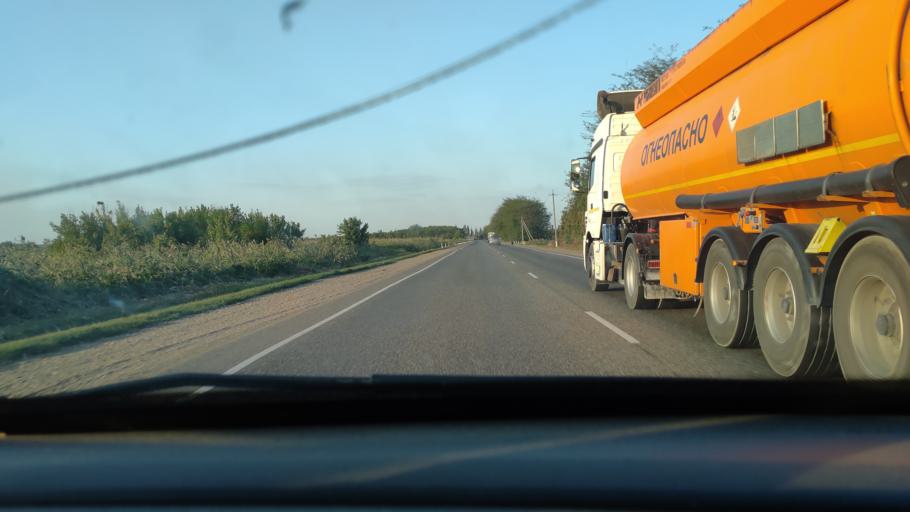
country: RU
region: Krasnodarskiy
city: Kanevskaya
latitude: 46.0662
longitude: 39.0085
